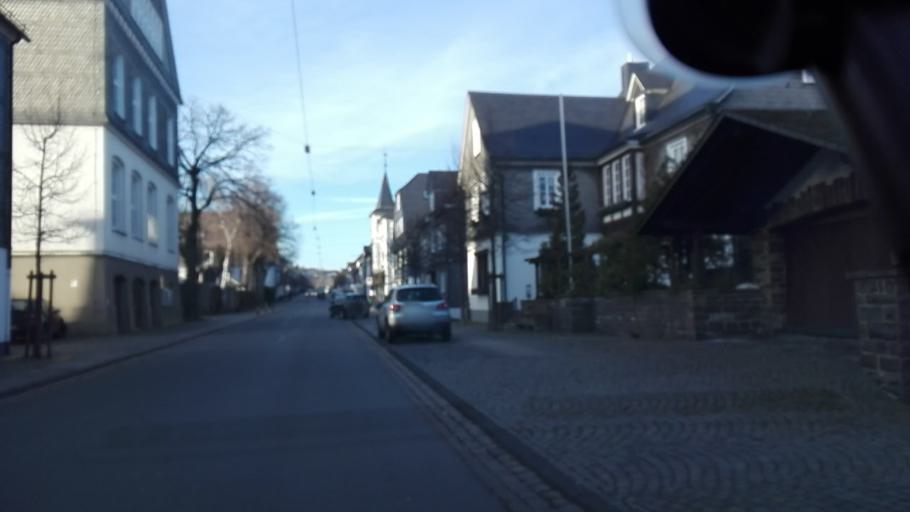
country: DE
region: North Rhine-Westphalia
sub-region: Regierungsbezirk Arnsberg
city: Schmallenberg
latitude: 51.1468
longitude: 8.2862
